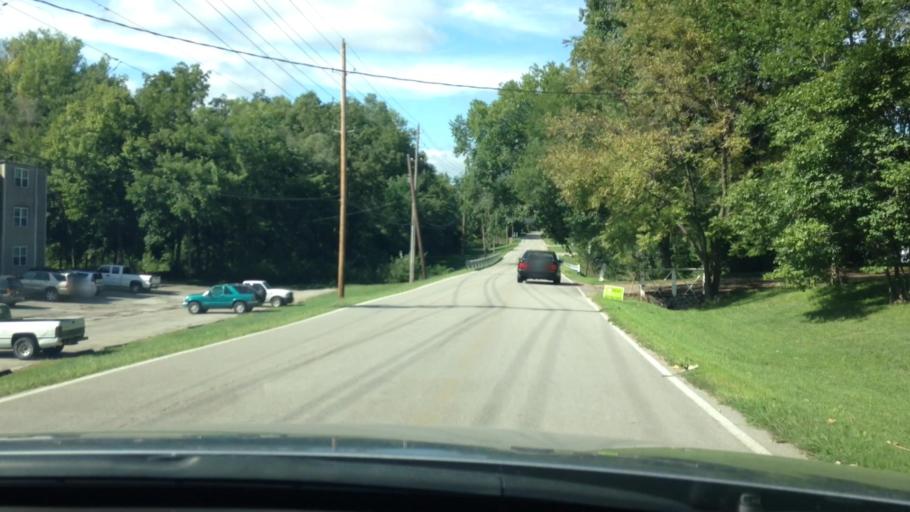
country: US
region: Missouri
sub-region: Platte County
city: Weatherby Lake
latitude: 39.3161
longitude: -94.6664
